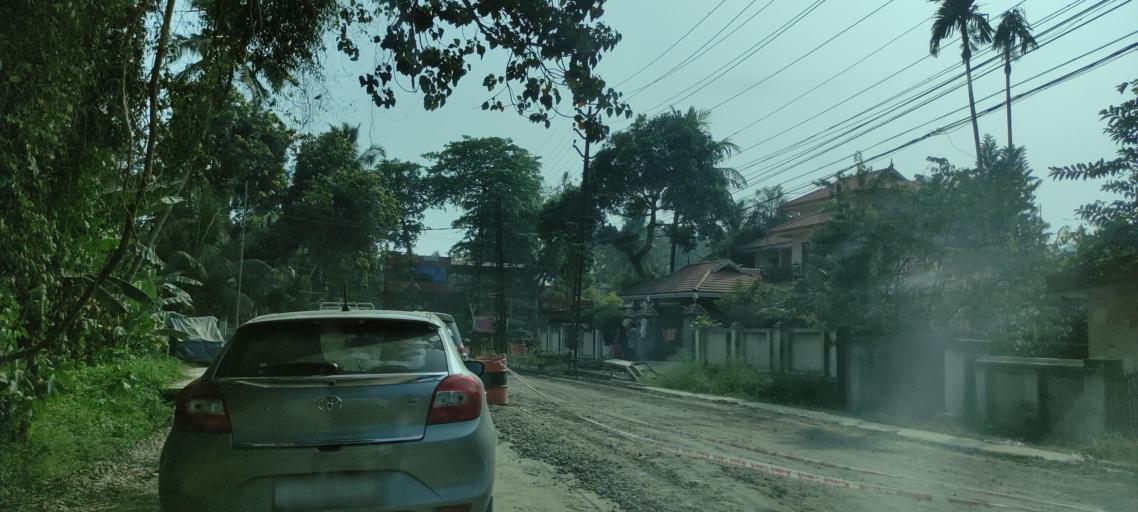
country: IN
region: Kerala
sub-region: Pattanamtitta
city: Tiruvalla
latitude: 9.3670
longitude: 76.5466
